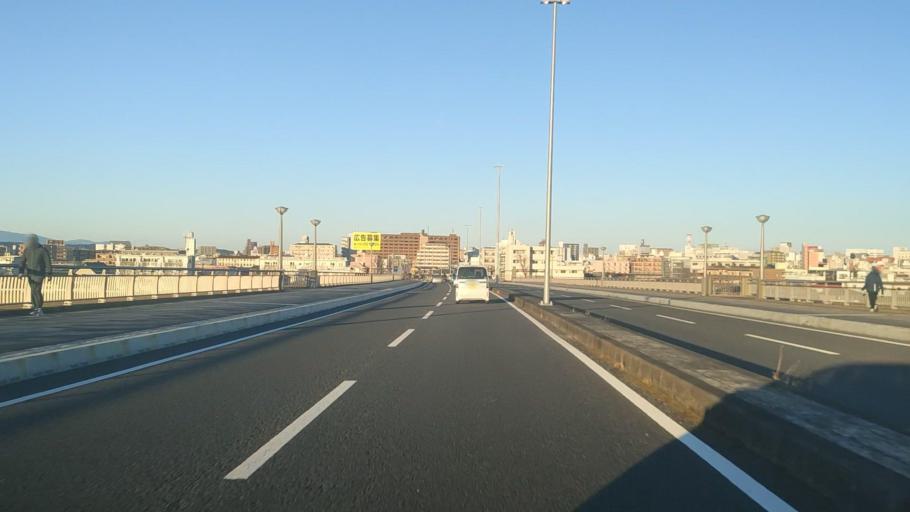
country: JP
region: Miyazaki
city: Miyazaki-shi
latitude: 31.9086
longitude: 131.4116
